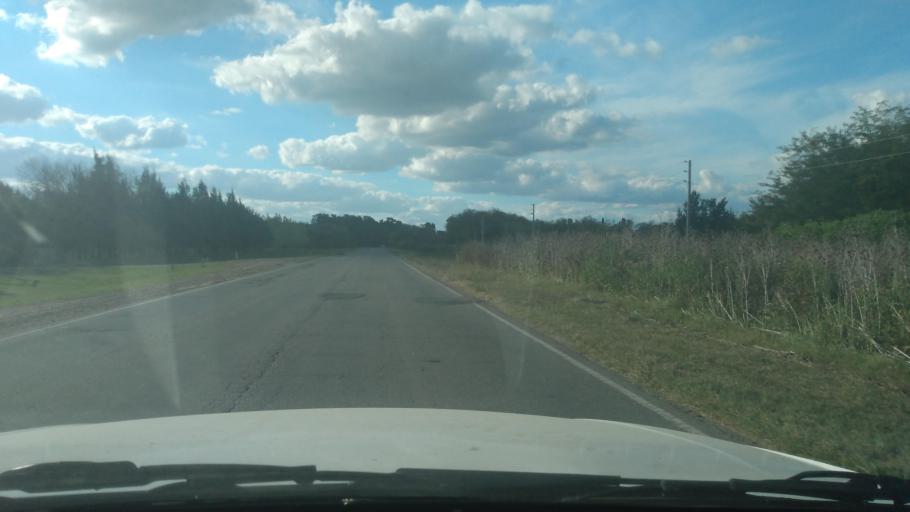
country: AR
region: Buenos Aires
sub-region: Partido de Mercedes
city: Mercedes
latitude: -34.6870
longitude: -59.4049
